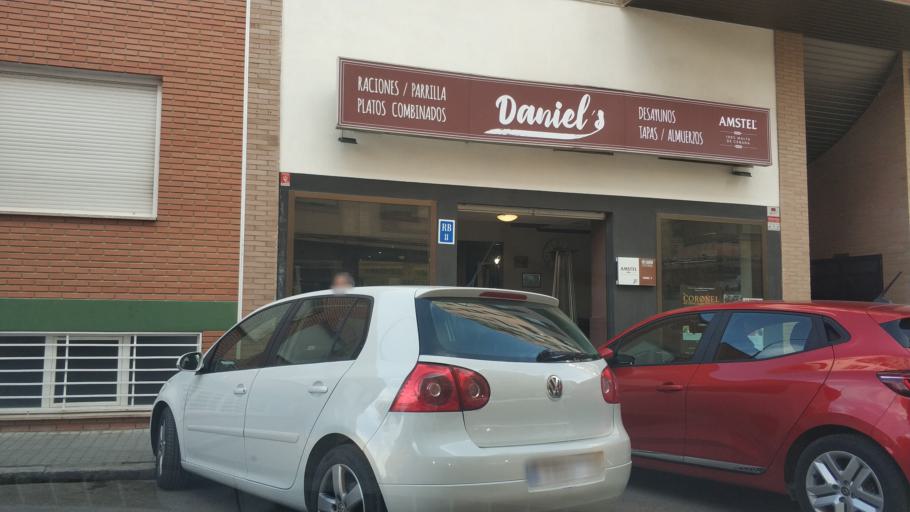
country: ES
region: Castille and Leon
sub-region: Provincia de Burgos
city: Aranda de Duero
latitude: 41.6734
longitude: -3.6841
